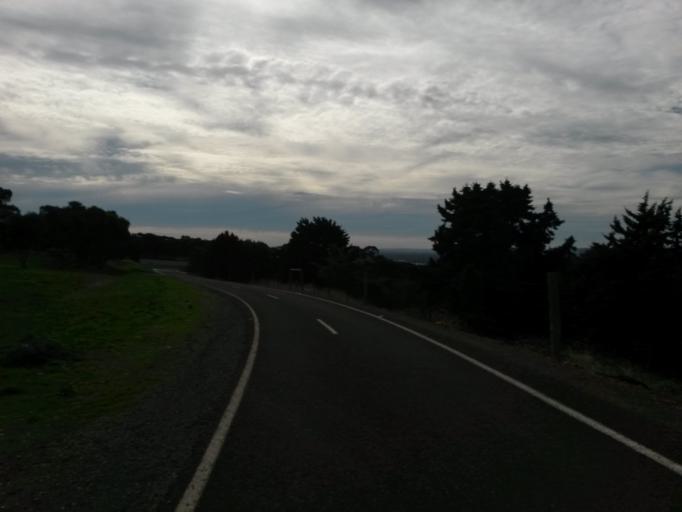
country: AU
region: South Australia
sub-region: Onkaparinga
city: Bedford Park
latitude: -35.0460
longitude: 138.5523
